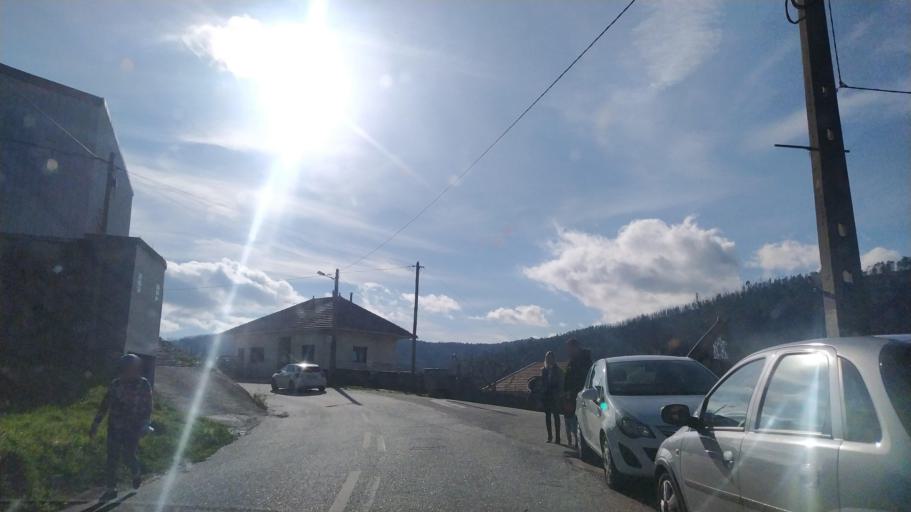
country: PT
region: Coimbra
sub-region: Oliveira do Hospital
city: Oliveira do Hospital
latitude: 40.2065
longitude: -7.7386
